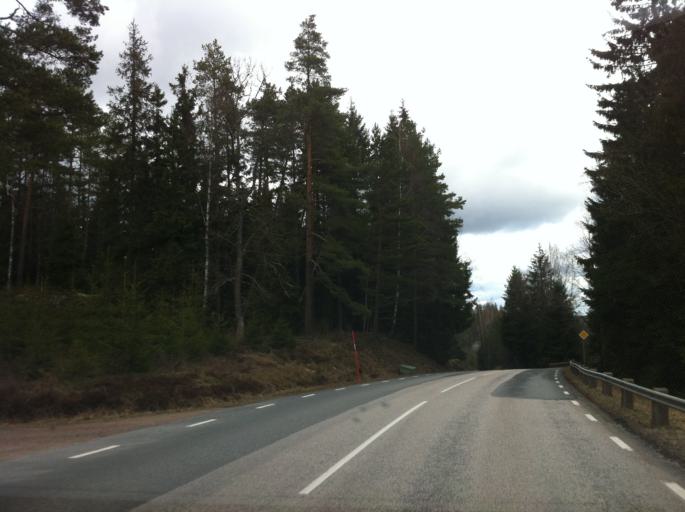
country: SE
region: Joenkoeping
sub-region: Gislaveds Kommun
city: Smalandsstenar
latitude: 57.2601
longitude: 13.2460
